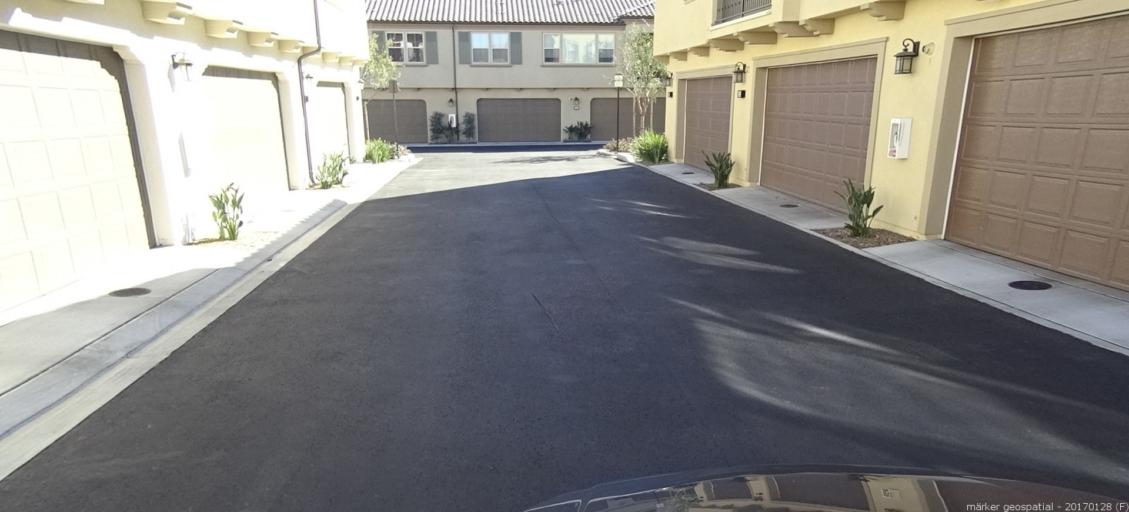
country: US
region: California
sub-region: Orange County
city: Foothill Ranch
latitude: 33.6702
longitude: -117.6758
